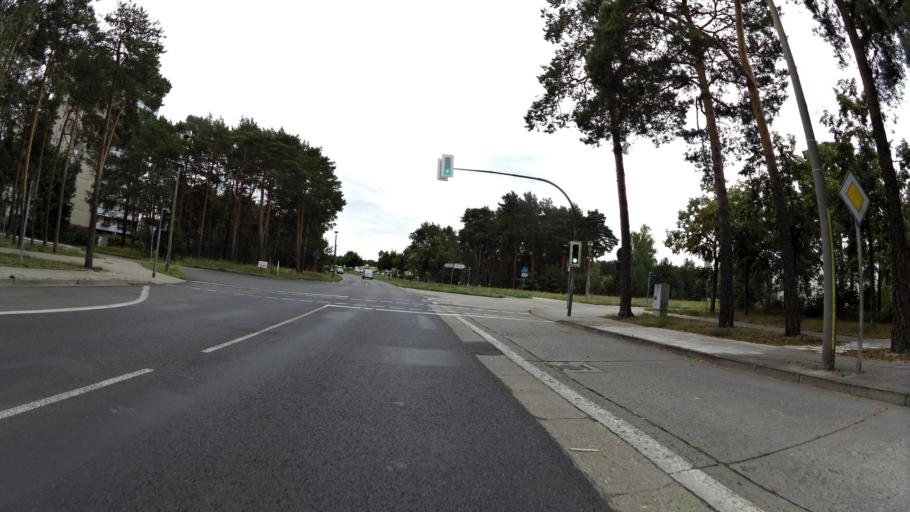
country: DE
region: Brandenburg
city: Eisenhuettenstadt
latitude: 52.1324
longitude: 14.6350
